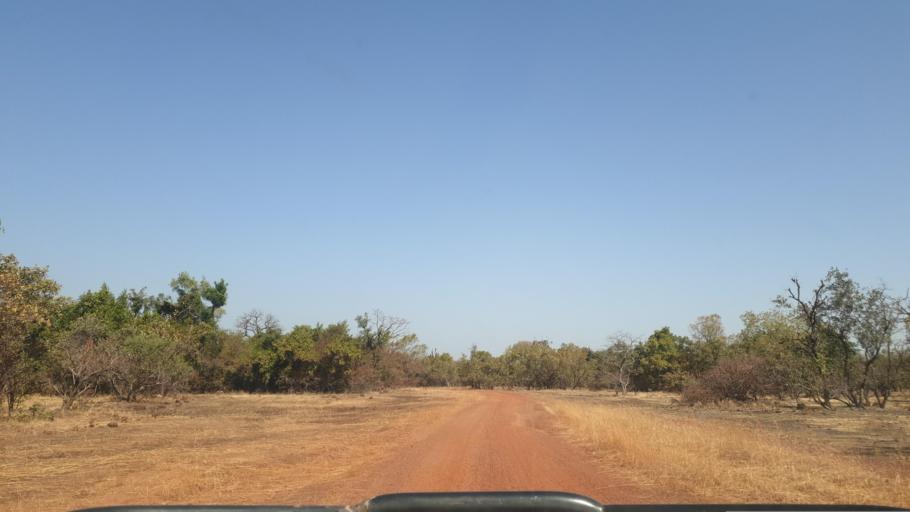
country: ML
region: Koulikoro
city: Dioila
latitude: 11.9180
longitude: -6.9842
